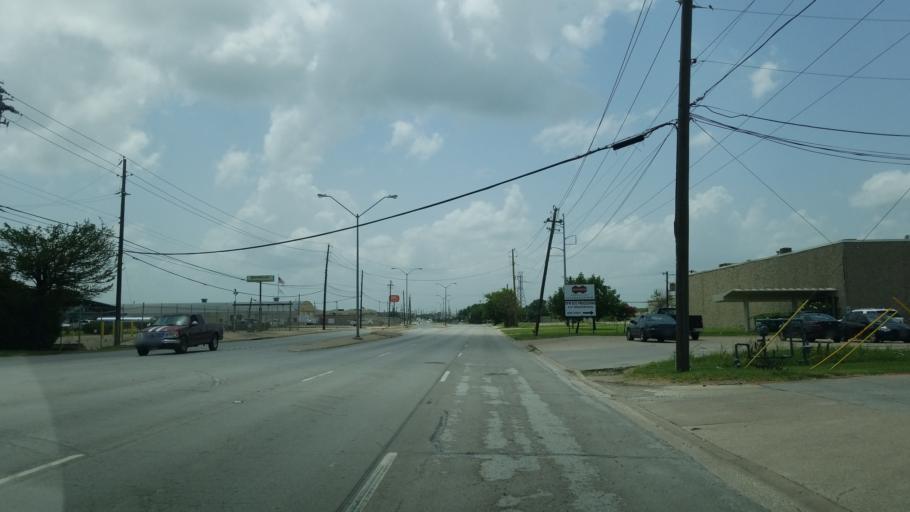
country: US
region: Texas
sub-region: Dallas County
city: Cockrell Hill
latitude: 32.7790
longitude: -96.8879
